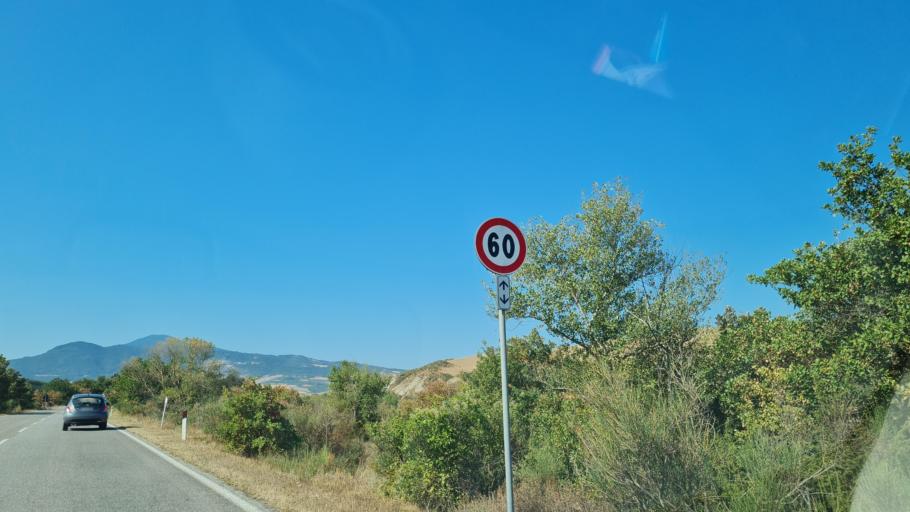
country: IT
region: Tuscany
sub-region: Provincia di Siena
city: Pienza
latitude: 42.9974
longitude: 11.7250
